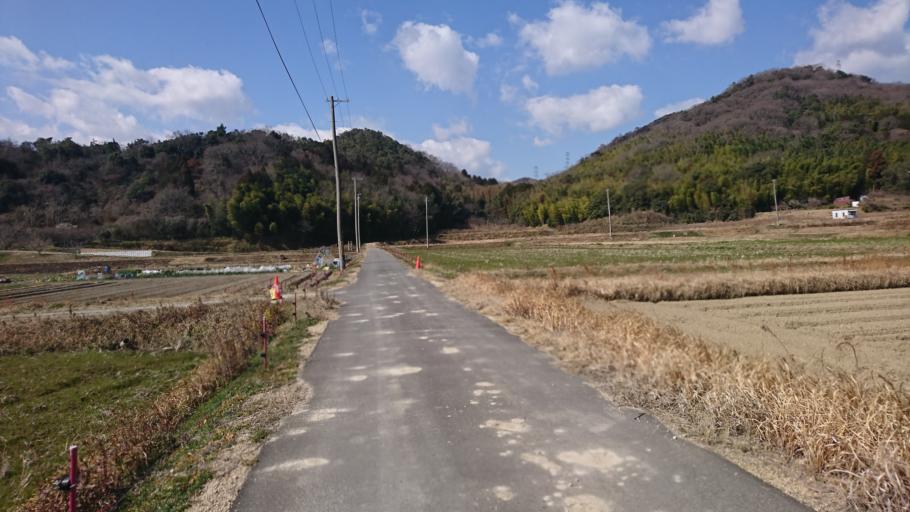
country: JP
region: Hyogo
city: Kakogawacho-honmachi
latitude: 34.8275
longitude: 134.8011
